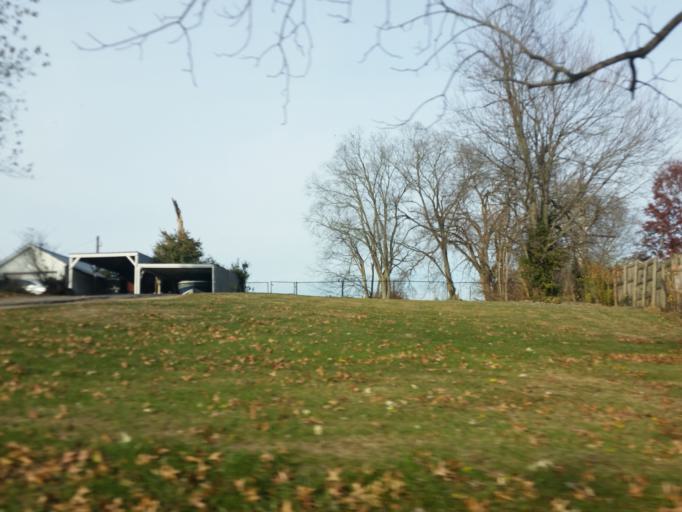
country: US
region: Kentucky
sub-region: Harrison County
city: Cynthiana
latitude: 38.3841
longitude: -84.2857
